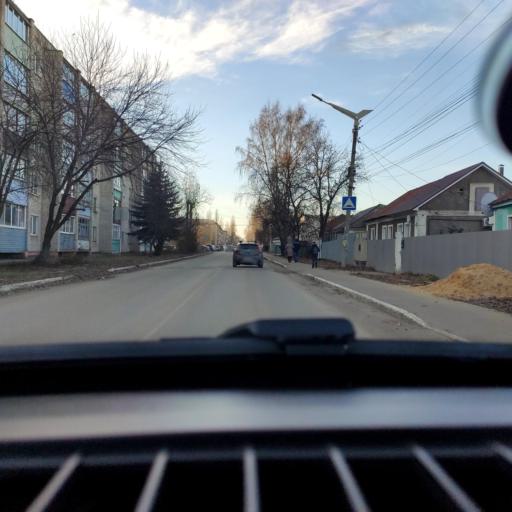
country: RU
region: Voronezj
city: Semiluki
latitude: 51.6970
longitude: 39.0218
